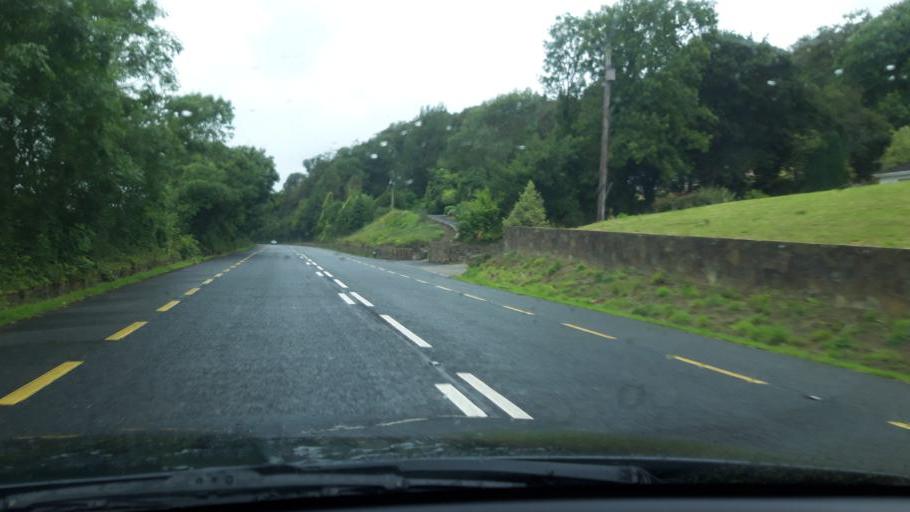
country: IE
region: Munster
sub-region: County Cork
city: Youghal
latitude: 52.1462
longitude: -7.8890
